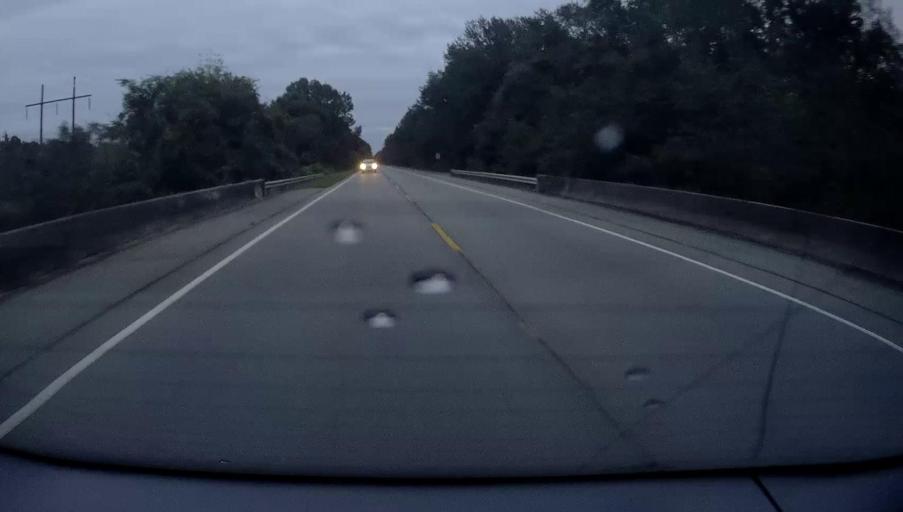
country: US
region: Georgia
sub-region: Houston County
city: Robins Air Force Base
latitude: 32.5421
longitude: -83.5295
